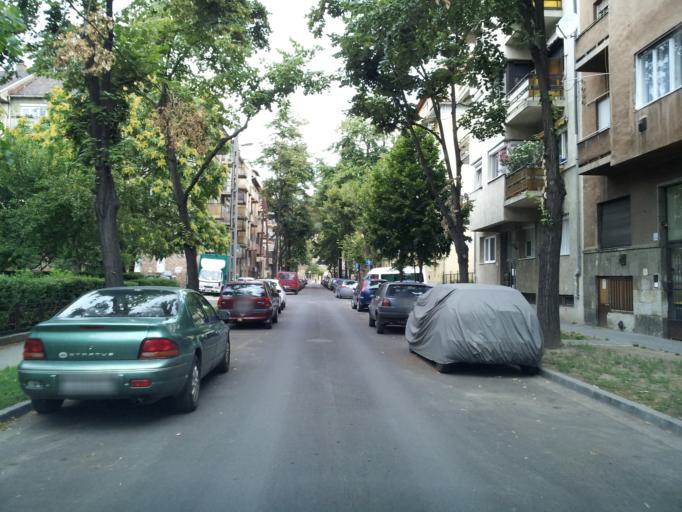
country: HU
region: Budapest
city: Budapest XIV. keruelet
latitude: 47.5048
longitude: 19.1046
